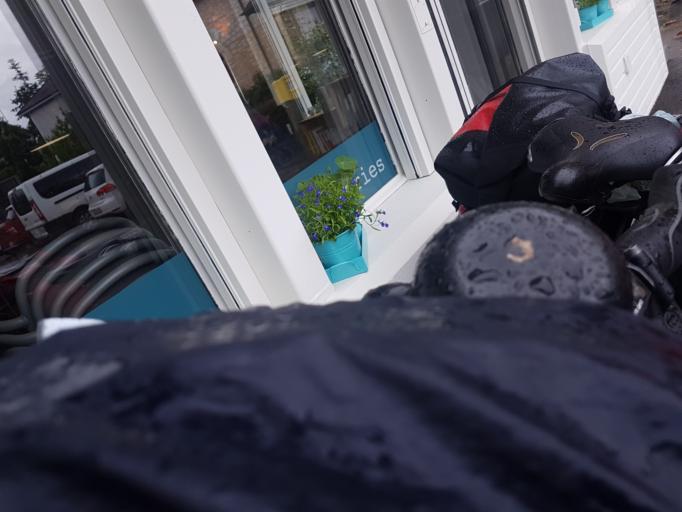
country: CH
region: Geneva
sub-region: Geneva
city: Dardagny
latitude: 46.1886
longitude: 6.0140
